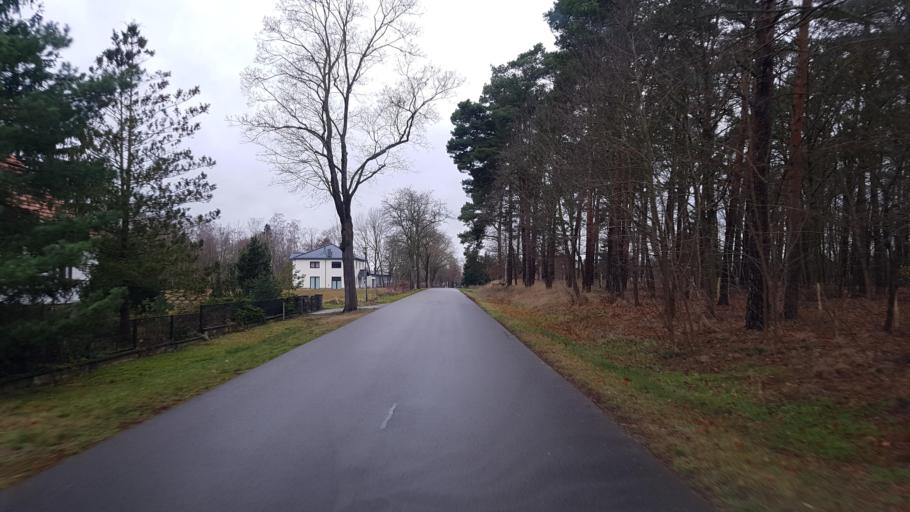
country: DE
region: Brandenburg
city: Tauche
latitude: 52.1055
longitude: 14.1310
